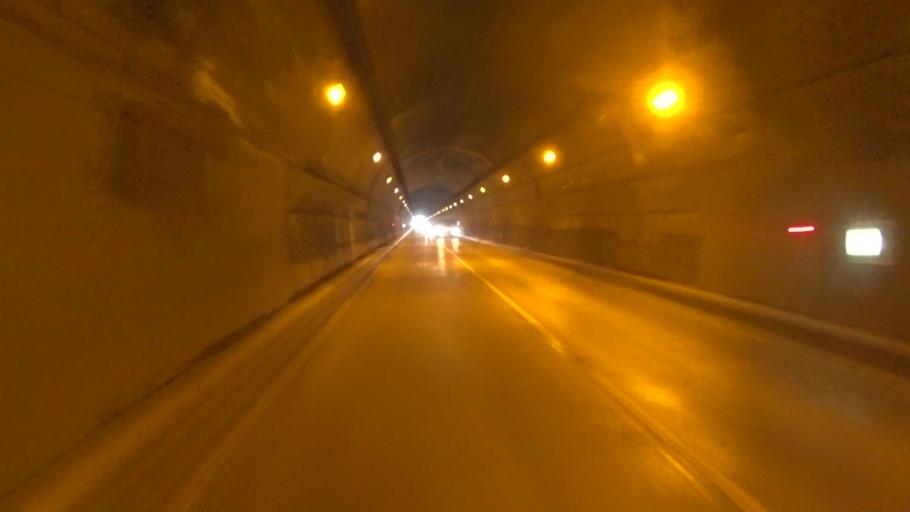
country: JP
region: Kyoto
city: Miyazu
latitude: 35.5518
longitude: 135.2221
